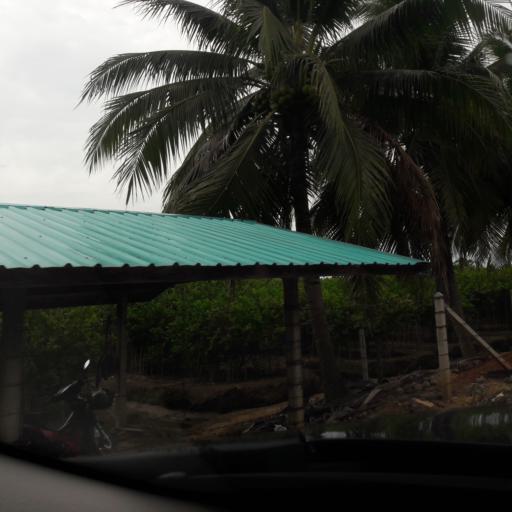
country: TH
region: Ratchaburi
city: Damnoen Saduak
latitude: 13.5693
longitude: 99.9386
